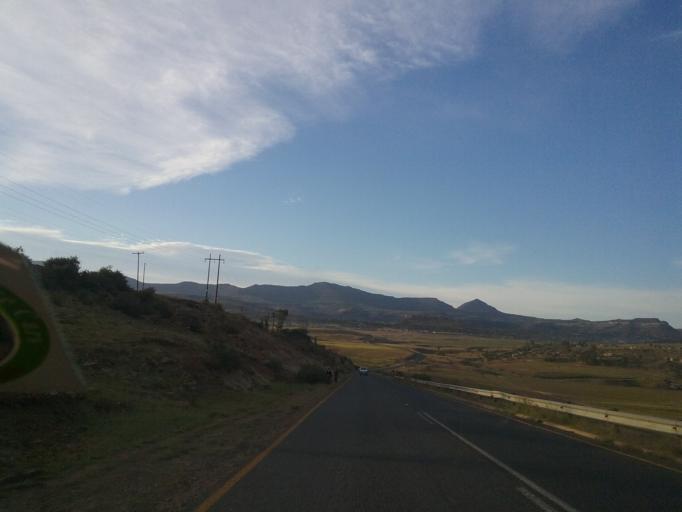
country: LS
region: Mohale's Hoek District
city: Mohale's Hoek
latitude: -30.1058
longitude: 27.4499
